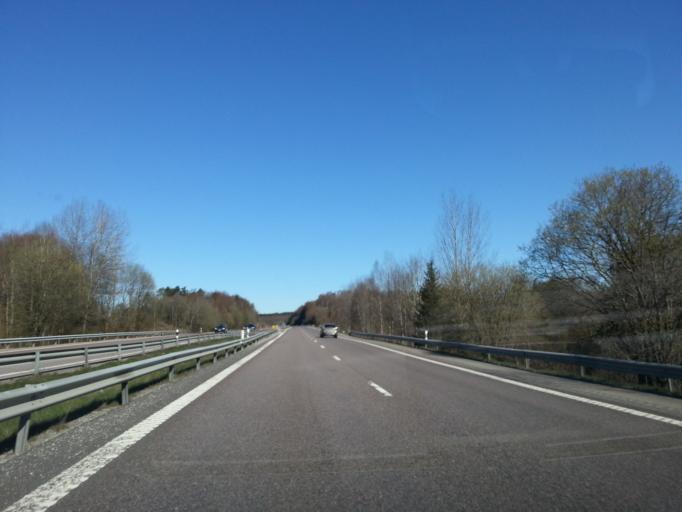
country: SE
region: Vaestra Goetaland
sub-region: Kungalvs Kommun
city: Kode
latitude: 57.9260
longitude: 11.8770
